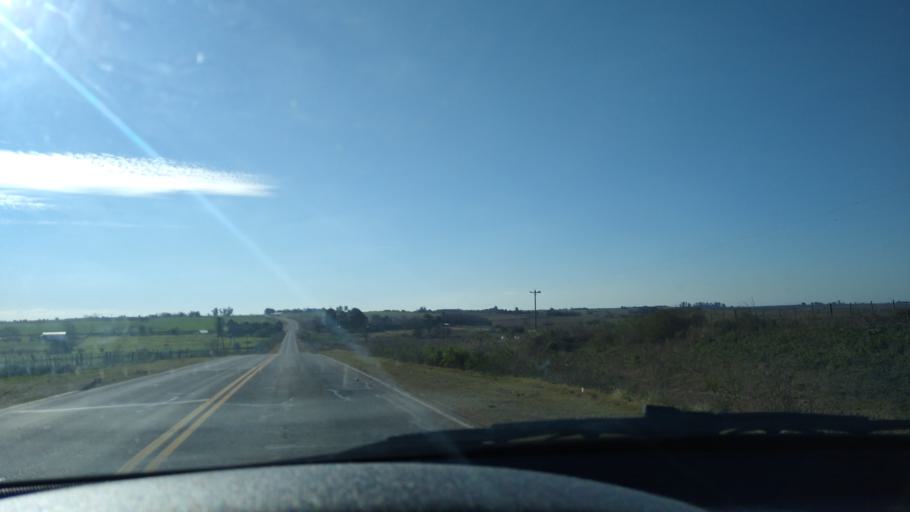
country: AR
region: Entre Rios
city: Aranguren
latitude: -32.4094
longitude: -60.3224
